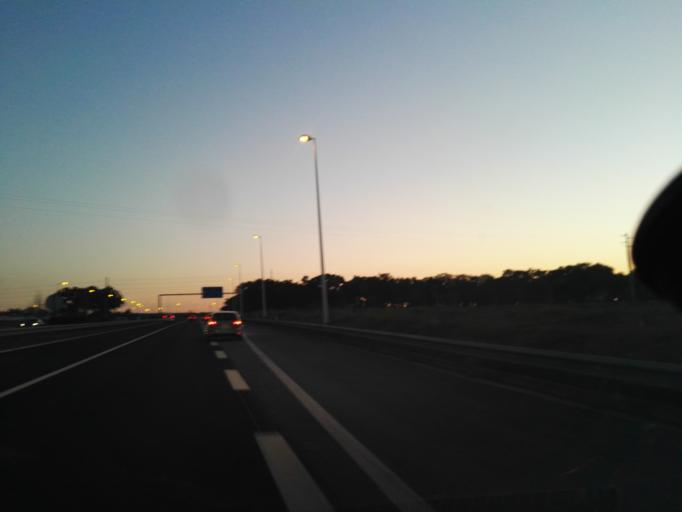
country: PT
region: Setubal
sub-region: Montijo
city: Montijo
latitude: 38.7226
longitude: -8.9400
